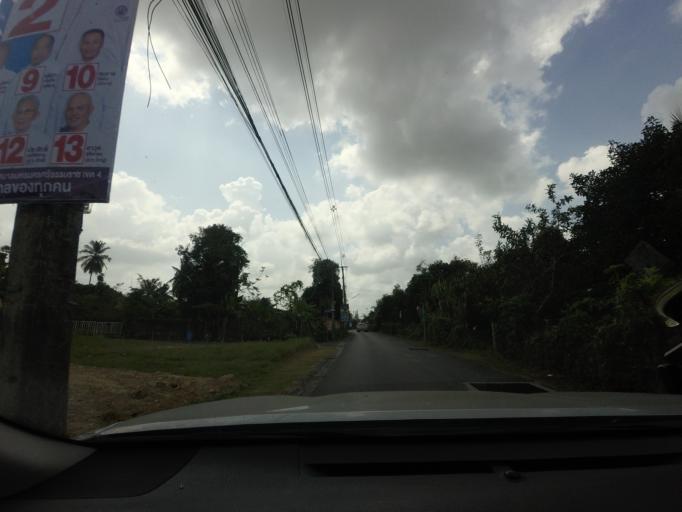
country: TH
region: Nakhon Si Thammarat
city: Nakhon Si Thammarat
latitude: 8.4369
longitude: 99.9307
